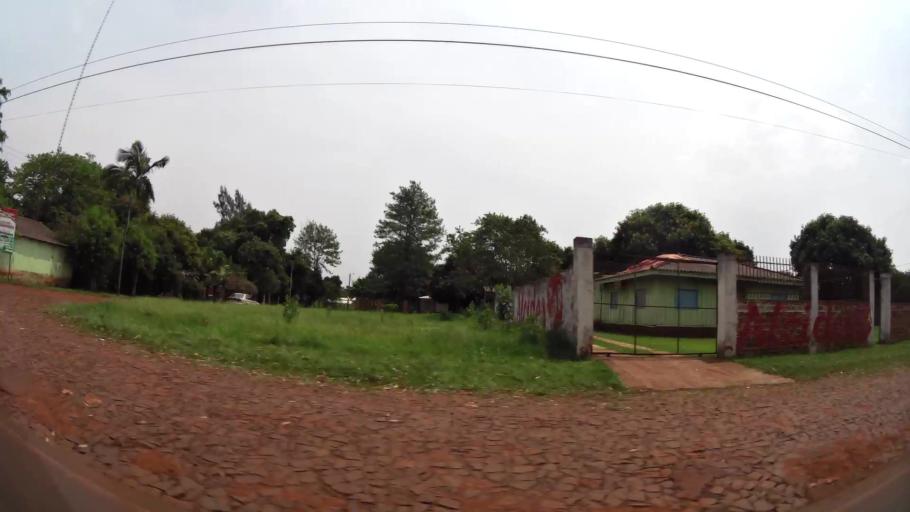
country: AR
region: Misiones
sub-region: Departamento de Iguazu
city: Puerto Iguazu
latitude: -25.5849
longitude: -54.6027
